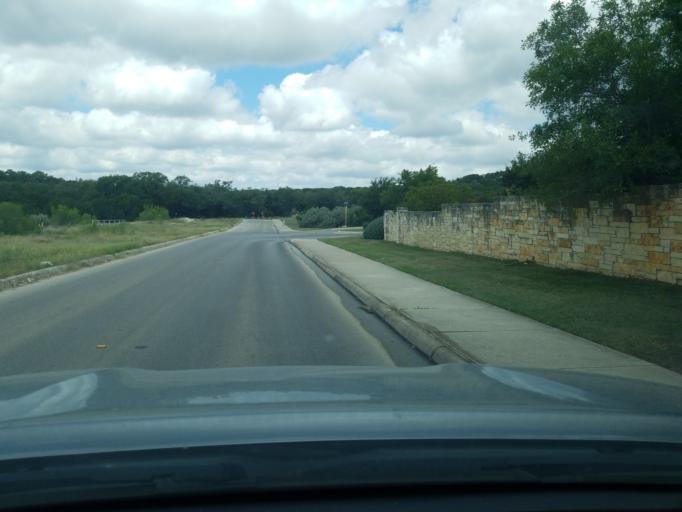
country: US
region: Texas
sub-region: Bexar County
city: Timberwood Park
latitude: 29.6621
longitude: -98.5099
